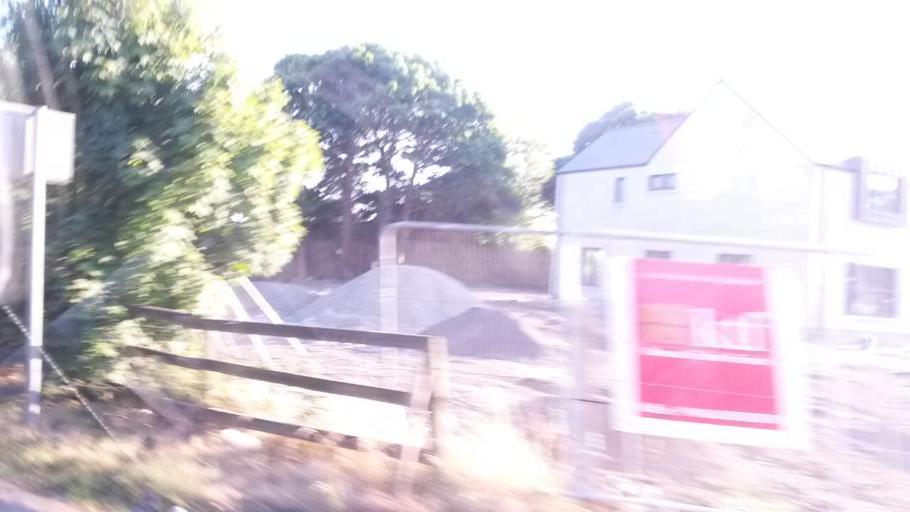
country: IE
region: Leinster
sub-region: An Mhi
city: Ashbourne
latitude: 53.5616
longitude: -6.3846
